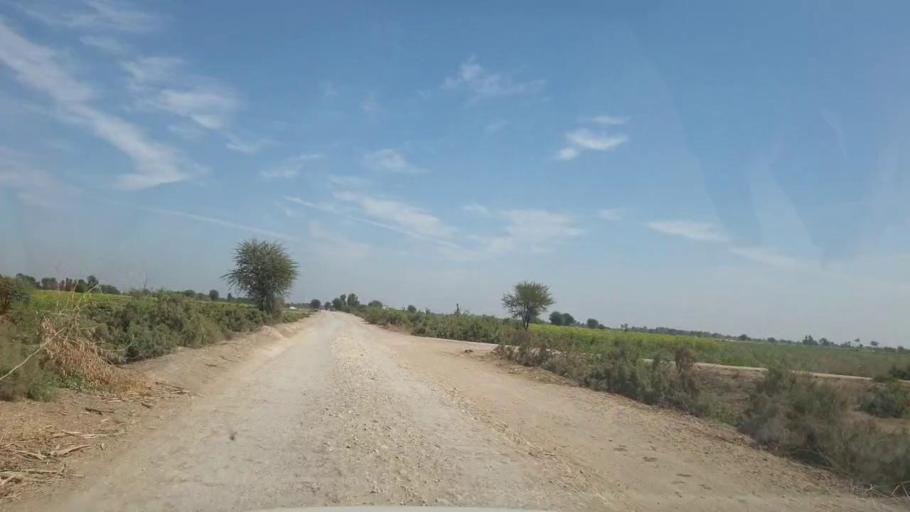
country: PK
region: Sindh
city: Mirpur Khas
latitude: 25.6058
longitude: 69.1884
